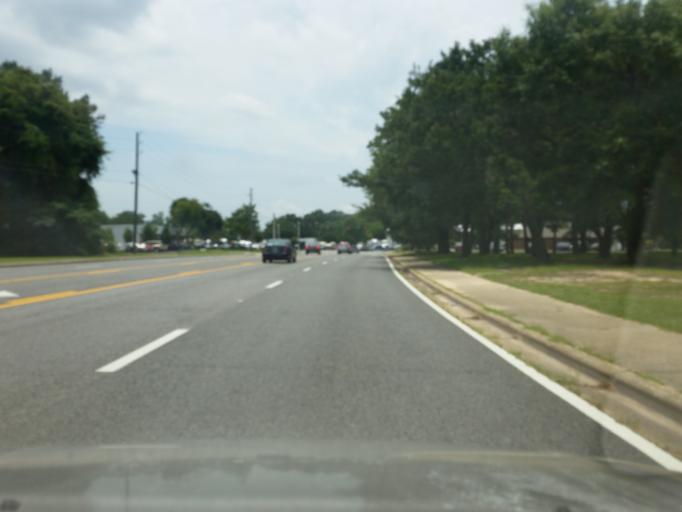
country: US
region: Florida
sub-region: Escambia County
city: Brent
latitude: 30.4722
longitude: -87.2529
